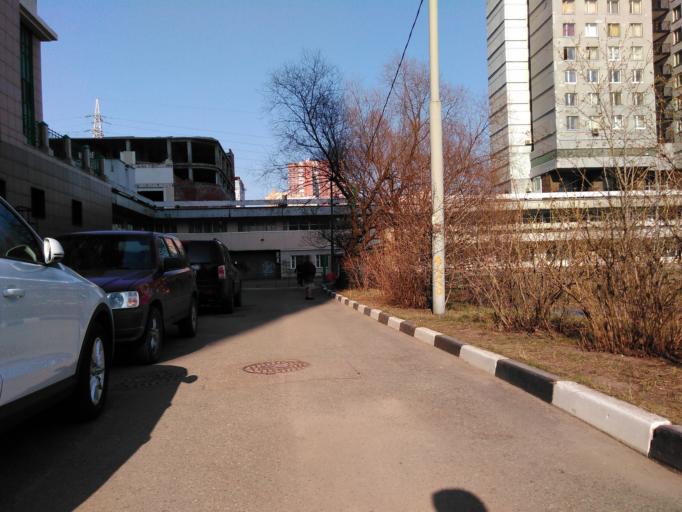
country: RU
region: Moscow
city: Ramenki
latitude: 55.6779
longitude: 37.5111
